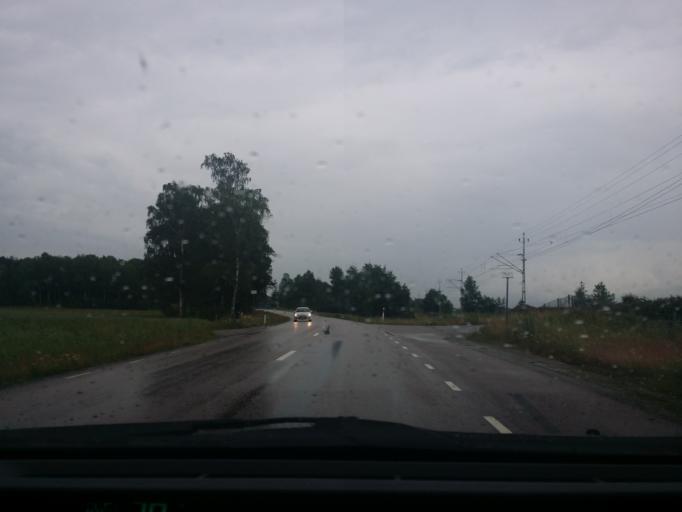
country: SE
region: Vaestmanland
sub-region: Arboga Kommun
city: Arboga
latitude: 59.4135
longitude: 15.7540
